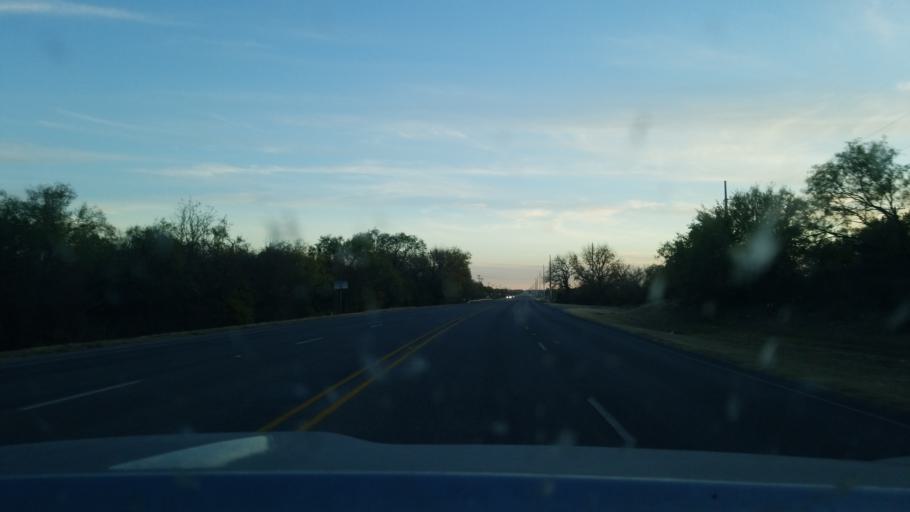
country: US
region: Texas
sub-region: Stephens County
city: Breckenridge
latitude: 32.7425
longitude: -98.9026
